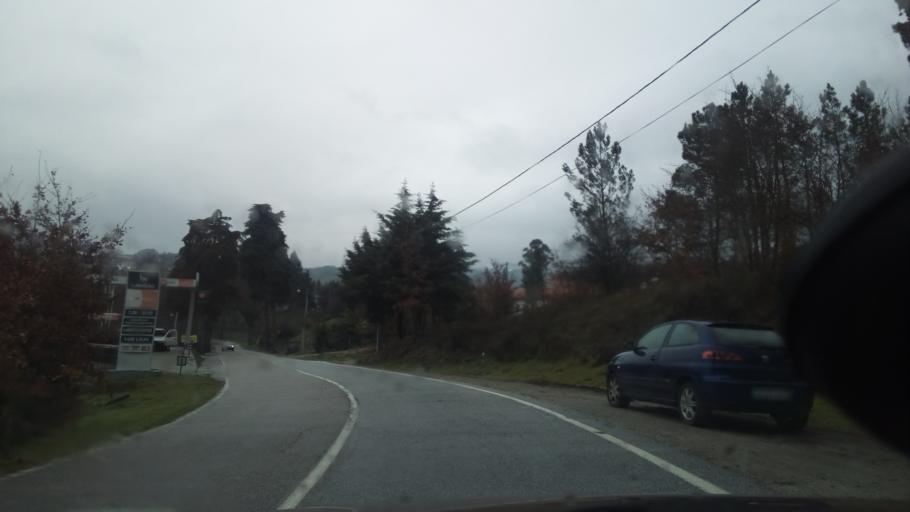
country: PT
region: Viseu
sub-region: Viseu
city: Rio de Loba
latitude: 40.6351
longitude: -7.8247
